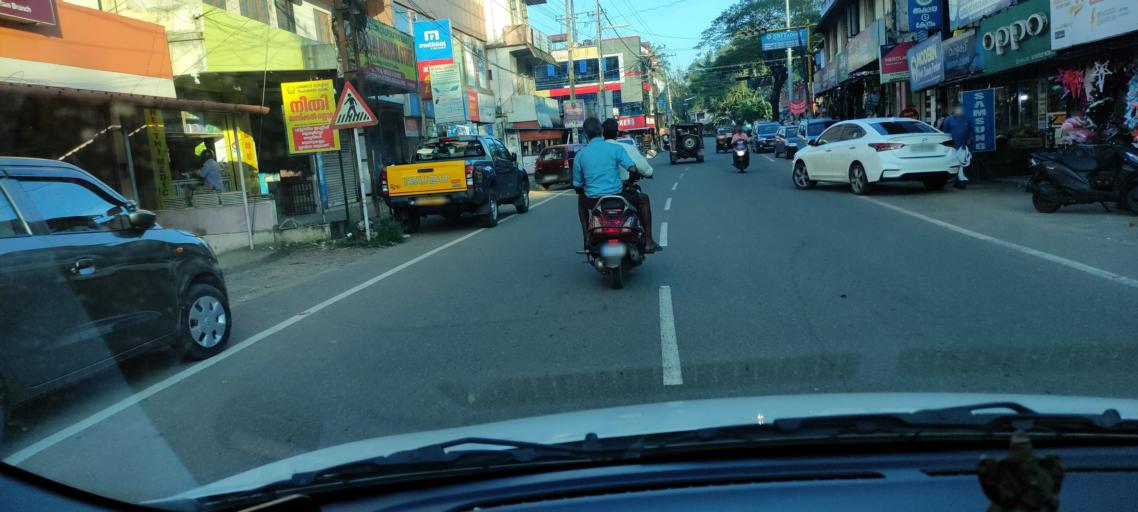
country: IN
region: Kerala
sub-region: Pattanamtitta
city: Adur
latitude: 9.1450
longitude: 76.7689
